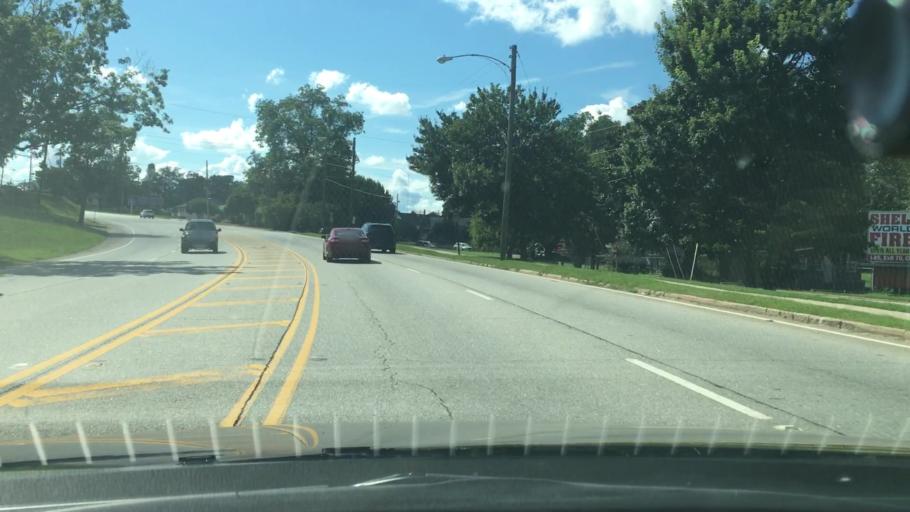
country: US
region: Georgia
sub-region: Spalding County
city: Griffin
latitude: 33.2466
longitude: -84.2547
